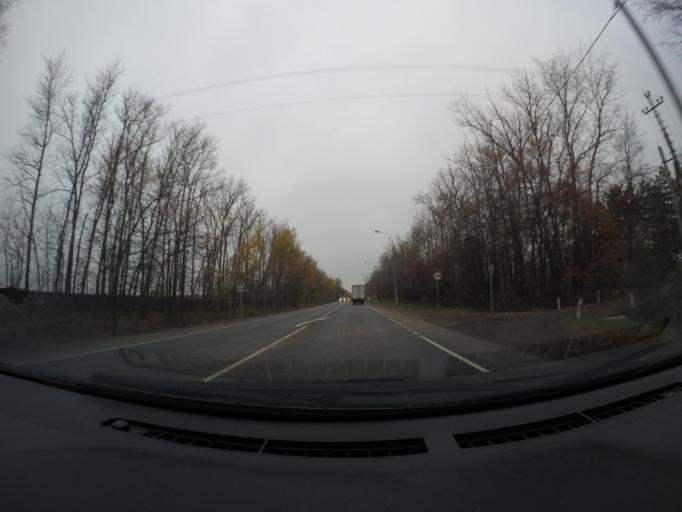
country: RU
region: Moskovskaya
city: Bronnitsy
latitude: 55.3747
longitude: 38.1509
